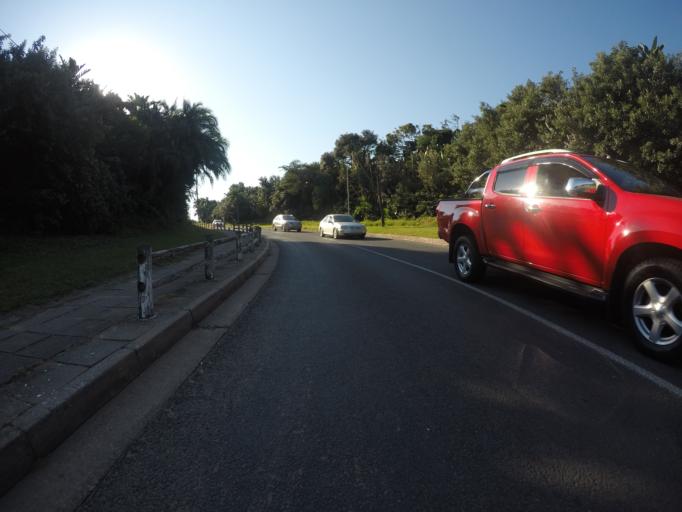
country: ZA
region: KwaZulu-Natal
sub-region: uThungulu District Municipality
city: Richards Bay
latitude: -28.7964
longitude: 32.0968
